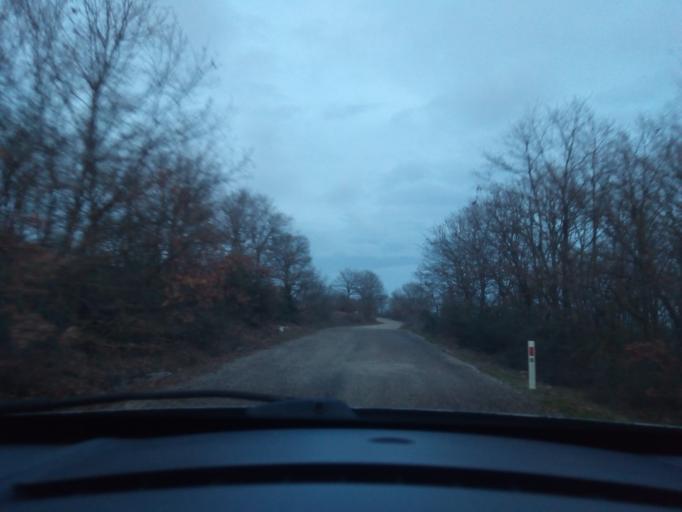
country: TR
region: Balikesir
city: Omerkoy
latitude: 39.9055
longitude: 28.0333
